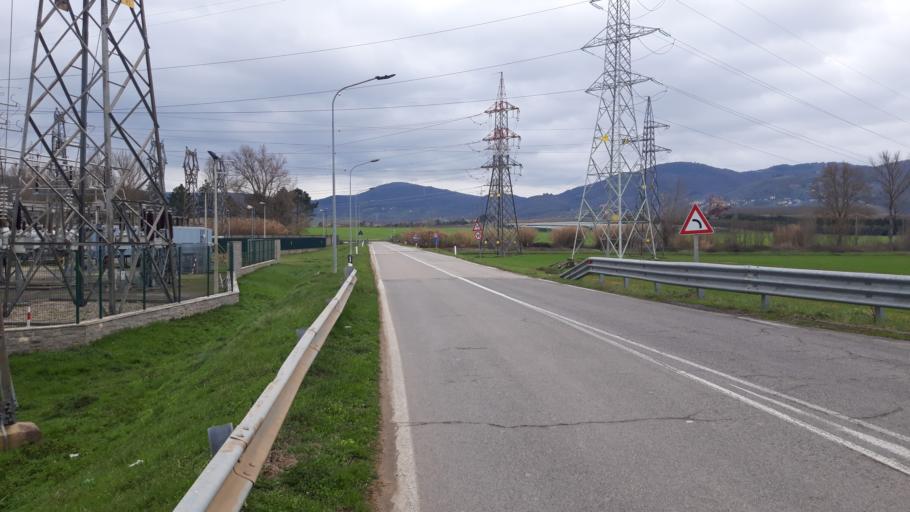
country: IT
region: Umbria
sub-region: Provincia di Perugia
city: Fontignano
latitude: 43.0047
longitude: 12.1796
